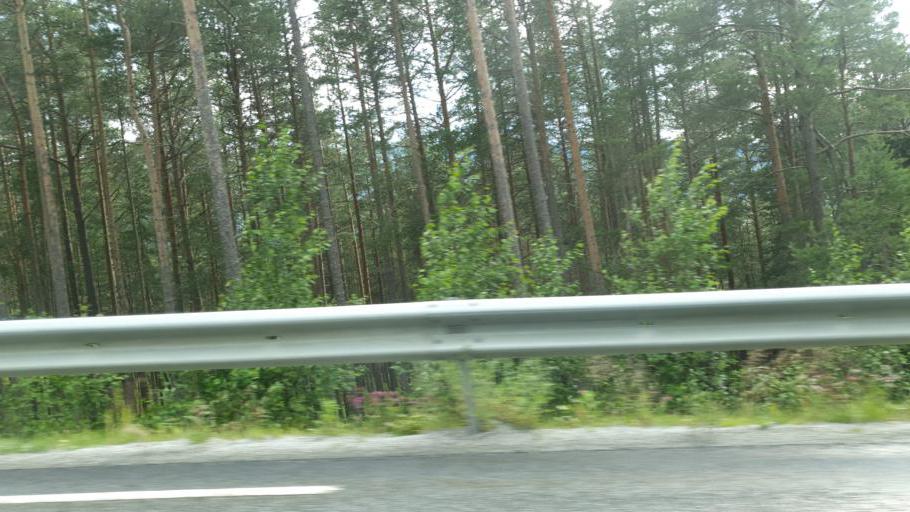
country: NO
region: Oppland
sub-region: Dovre
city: Dovre
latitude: 61.8623
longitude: 9.2314
